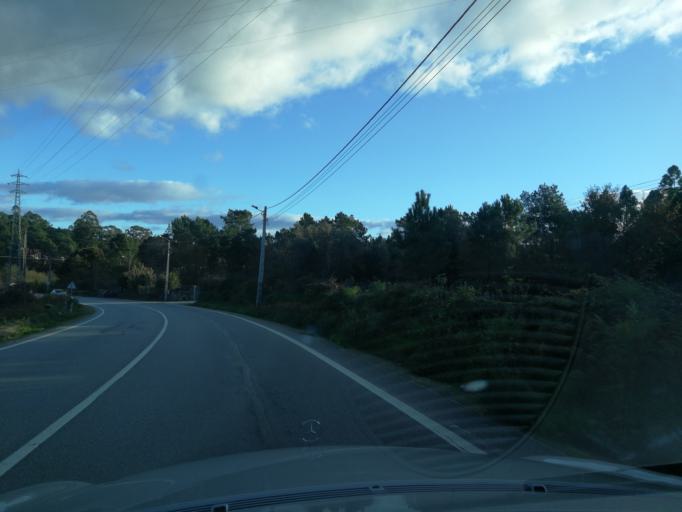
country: PT
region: Braga
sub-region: Esposende
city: Marinhas
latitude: 41.6170
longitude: -8.7549
